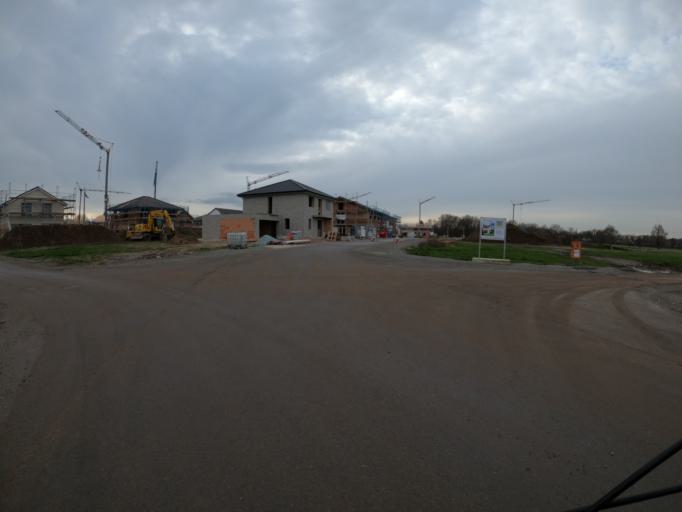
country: DE
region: North Rhine-Westphalia
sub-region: Regierungsbezirk Arnsberg
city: Lippstadt
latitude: 51.6866
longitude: 8.3311
